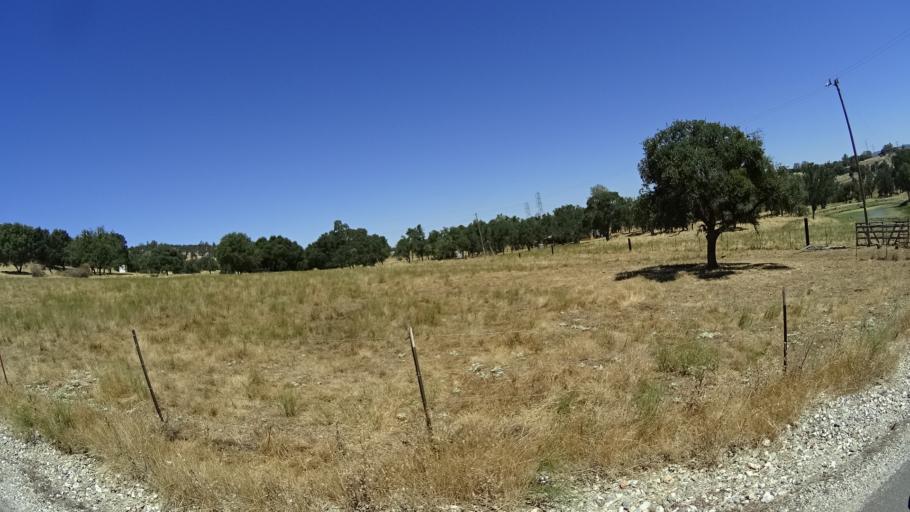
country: US
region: California
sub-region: Calaveras County
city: Copperopolis
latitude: 37.9502
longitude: -120.6882
